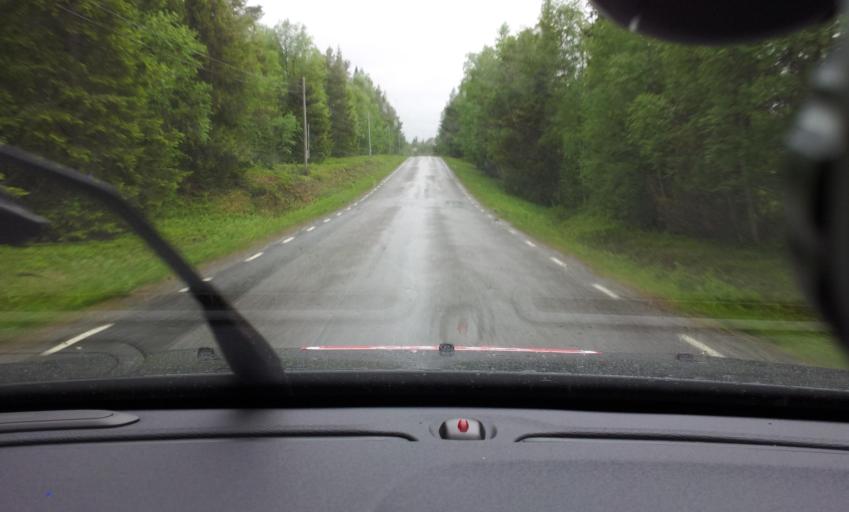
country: SE
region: Jaemtland
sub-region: Are Kommun
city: Are
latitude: 63.1555
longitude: 13.0185
